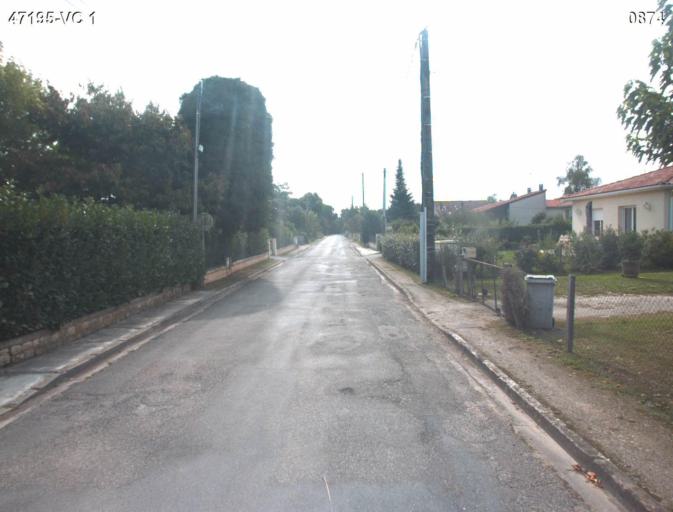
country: FR
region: Aquitaine
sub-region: Departement du Lot-et-Garonne
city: Nerac
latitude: 44.1253
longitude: 0.3453
